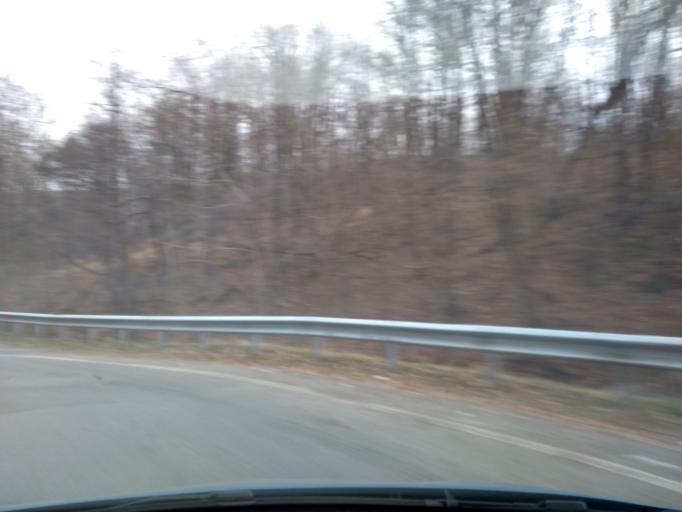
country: IT
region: Piedmont
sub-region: Provincia di Torino
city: Germagnano
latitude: 45.2604
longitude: 7.4557
